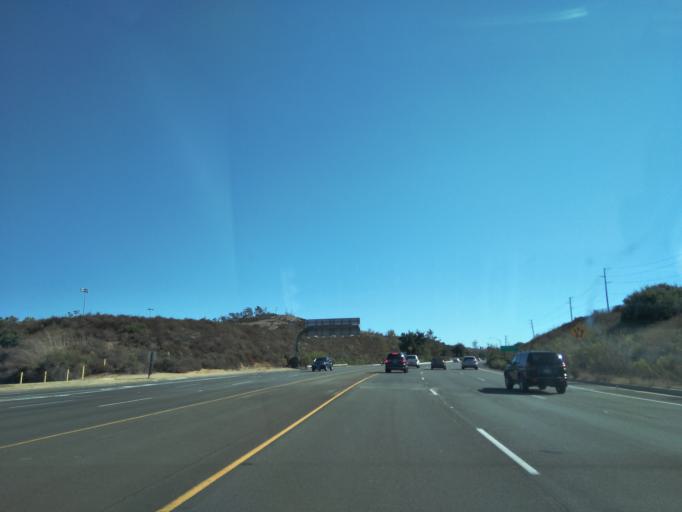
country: US
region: California
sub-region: Orange County
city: San Joaquin Hills
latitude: 33.6195
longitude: -117.8264
